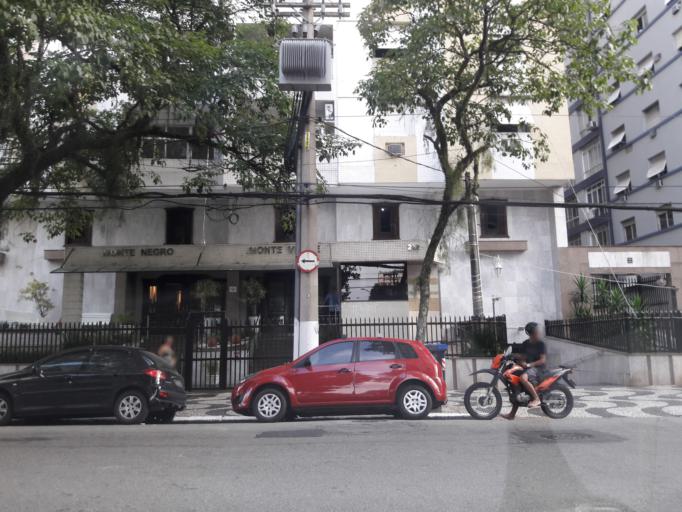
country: BR
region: Sao Paulo
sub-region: Santos
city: Santos
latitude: -23.9665
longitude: -46.3411
